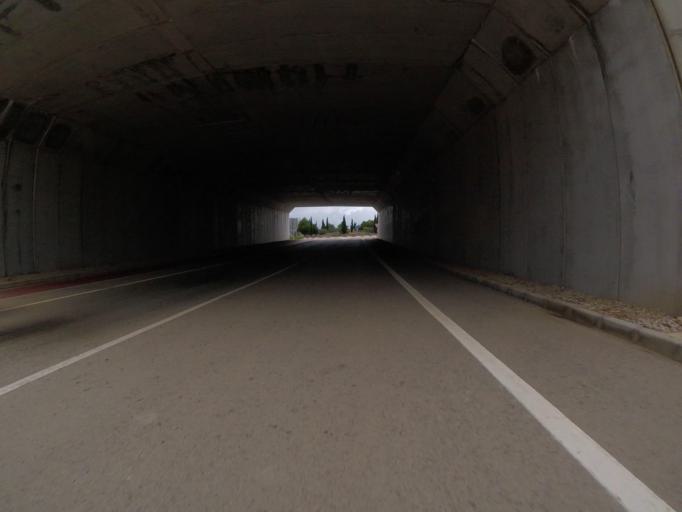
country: ES
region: Valencia
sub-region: Provincia de Castello
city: Benlloch
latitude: 40.1960
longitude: 0.0533
